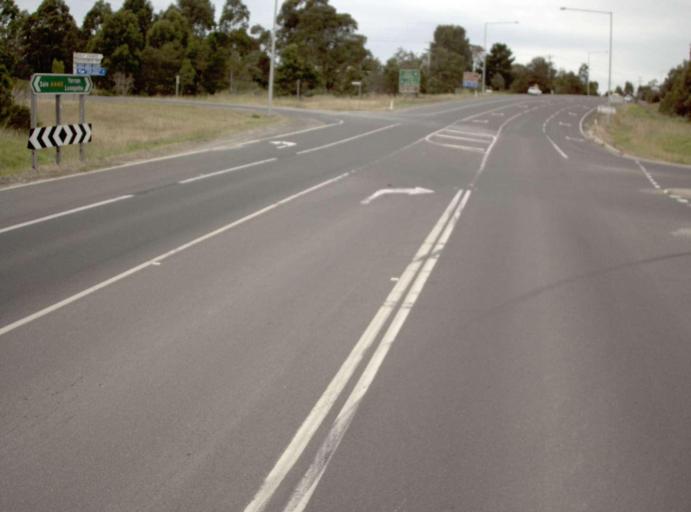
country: AU
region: Victoria
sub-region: Wellington
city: Sale
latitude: -38.1592
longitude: 147.0848
